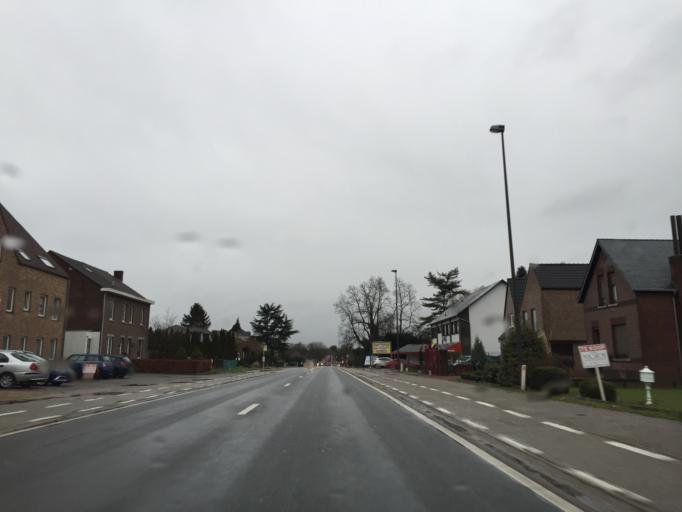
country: BE
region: Flanders
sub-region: Provincie Limburg
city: Lanaken
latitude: 50.8867
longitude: 5.6735
